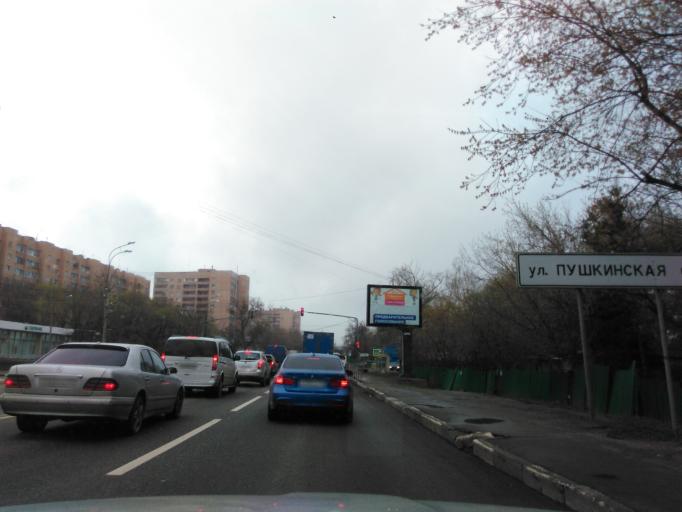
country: RU
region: Moskovskaya
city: Krasnogorsk
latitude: 55.8269
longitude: 37.3112
